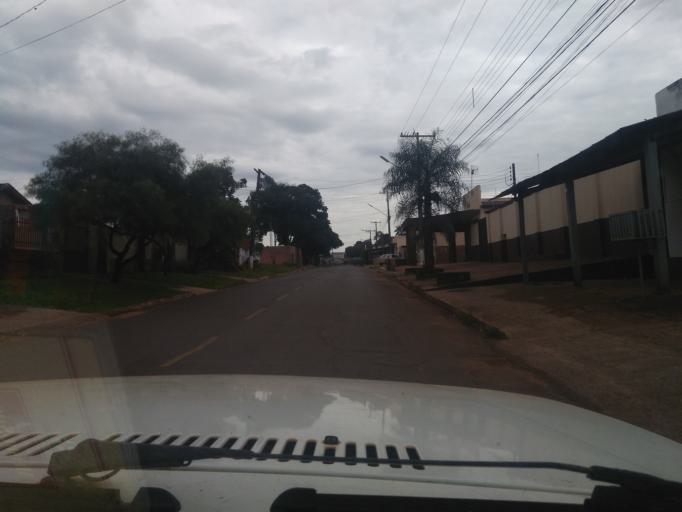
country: BR
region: Mato Grosso do Sul
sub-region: Ponta Pora
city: Ponta Pora
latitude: -22.5179
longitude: -55.7360
